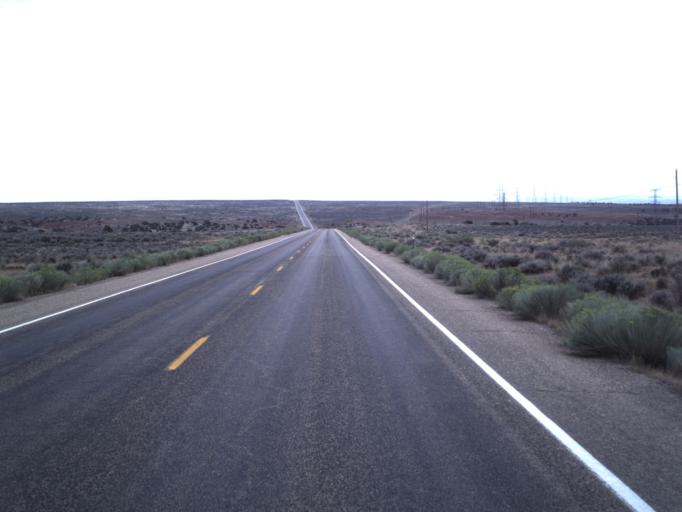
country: US
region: Utah
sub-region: Uintah County
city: Naples
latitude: 40.1719
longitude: -109.3198
